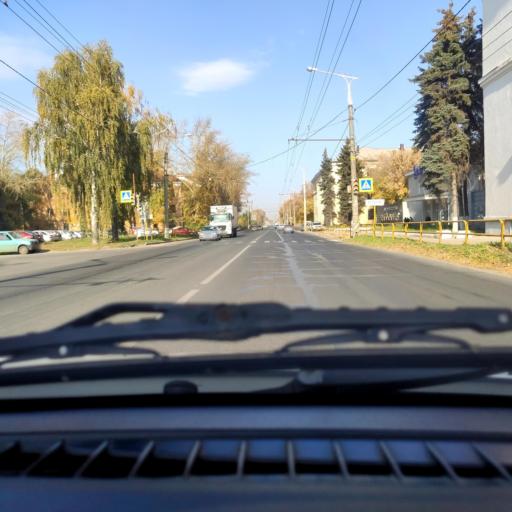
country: RU
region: Samara
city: Tol'yatti
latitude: 53.5226
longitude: 49.4337
